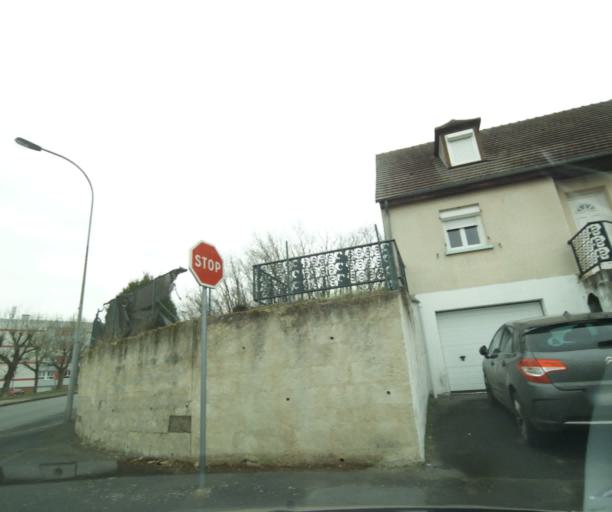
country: FR
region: Picardie
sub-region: Departement de l'Oise
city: Noyon
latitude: 49.5818
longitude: 3.0214
